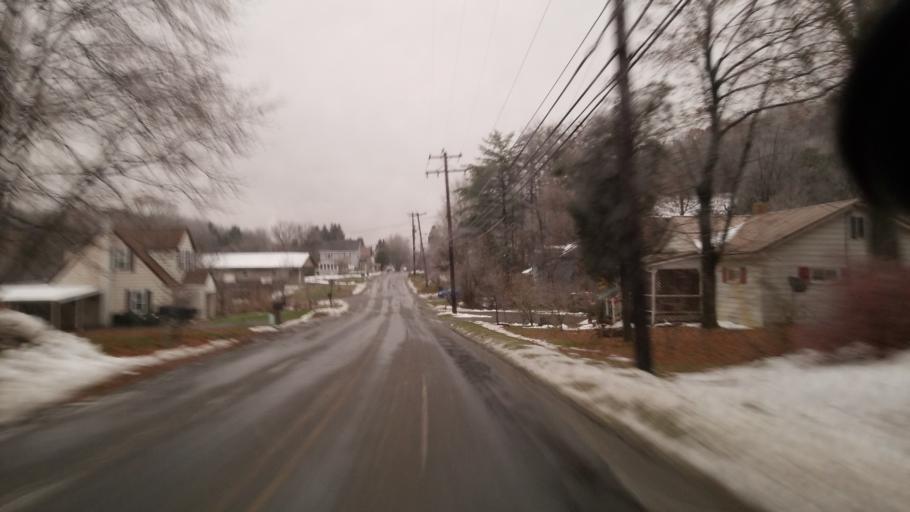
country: US
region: Pennsylvania
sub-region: Clearfield County
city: Clearfield
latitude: 41.0408
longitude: -78.4578
